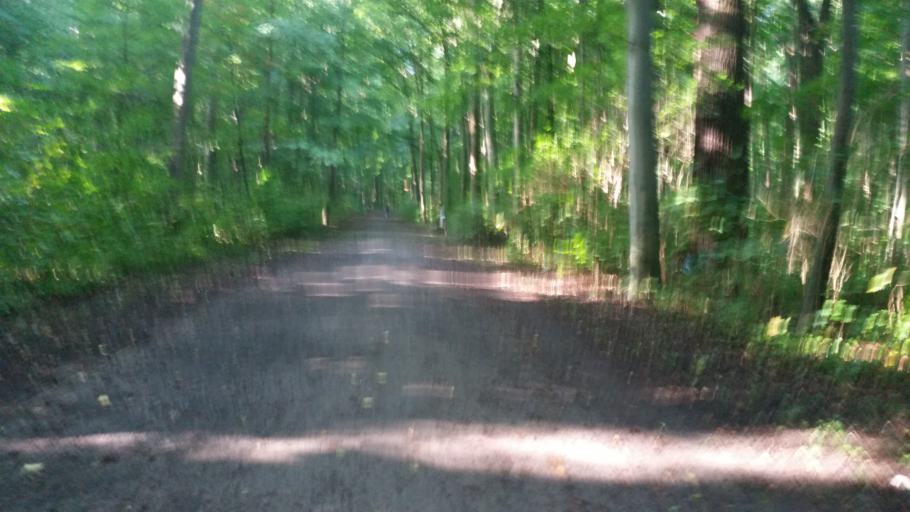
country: DE
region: Lower Saxony
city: Hannover
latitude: 52.3826
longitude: 9.7611
